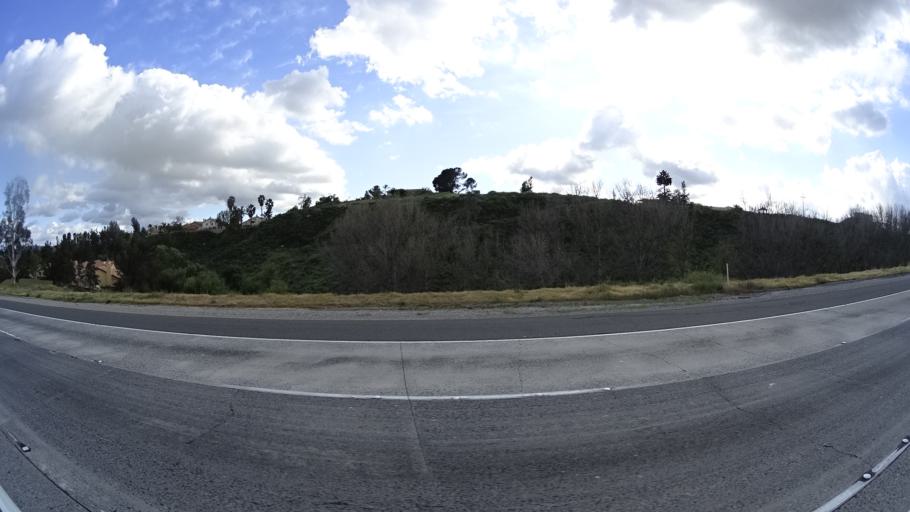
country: US
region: California
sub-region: Riverside County
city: Murrieta
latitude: 33.5826
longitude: -117.2297
